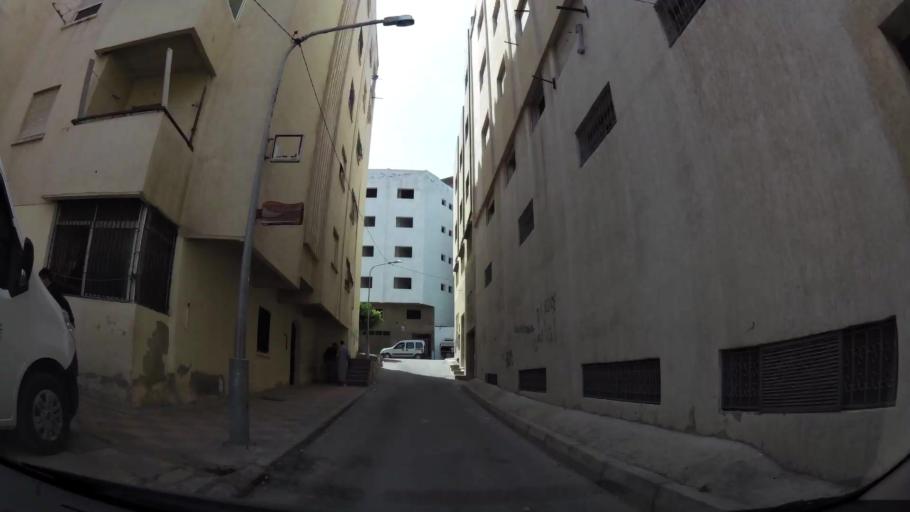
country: MA
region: Tanger-Tetouan
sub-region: Tanger-Assilah
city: Tangier
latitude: 35.7472
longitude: -5.8370
